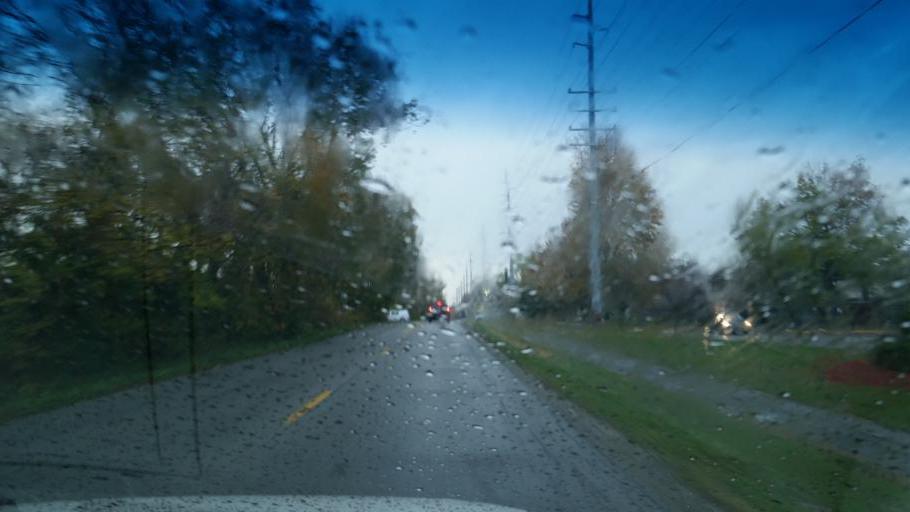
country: US
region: Indiana
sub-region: Howard County
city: Kokomo
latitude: 40.4631
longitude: -86.1460
